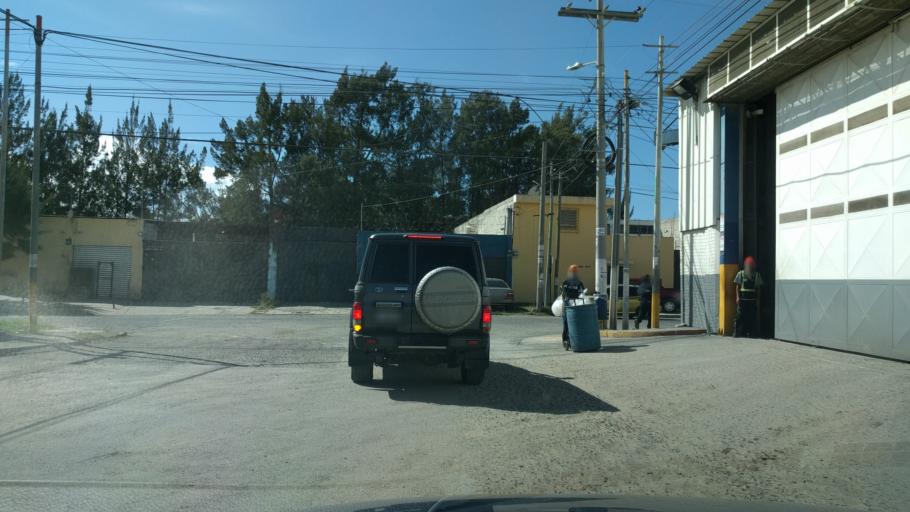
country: GT
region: Guatemala
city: Villa Nueva
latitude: 14.5801
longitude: -90.5641
